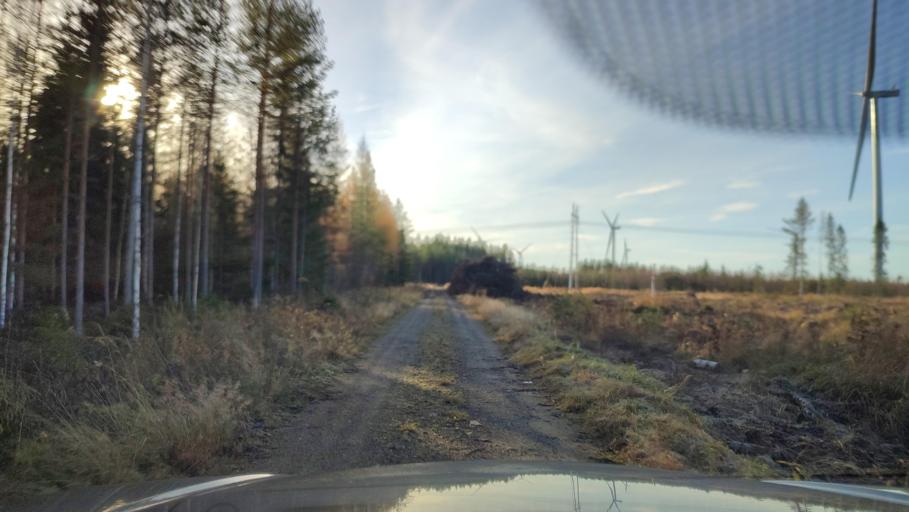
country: FI
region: Southern Ostrobothnia
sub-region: Suupohja
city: Karijoki
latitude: 62.1815
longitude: 21.6087
